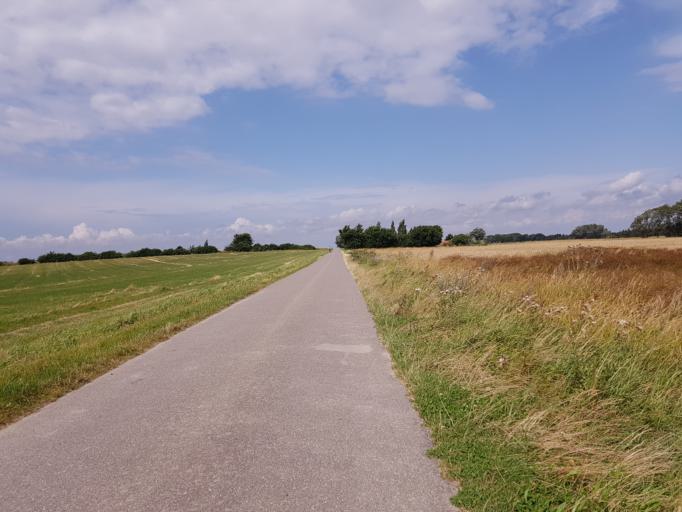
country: DK
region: Zealand
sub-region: Guldborgsund Kommune
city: Nykobing Falster
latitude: 54.5818
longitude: 11.9594
